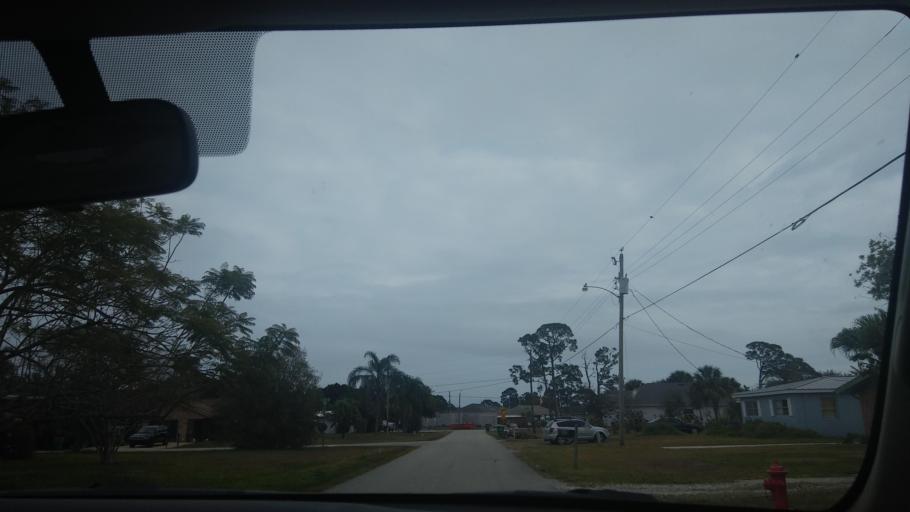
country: US
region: Florida
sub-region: Indian River County
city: Sebastian
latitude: 27.7974
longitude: -80.4853
